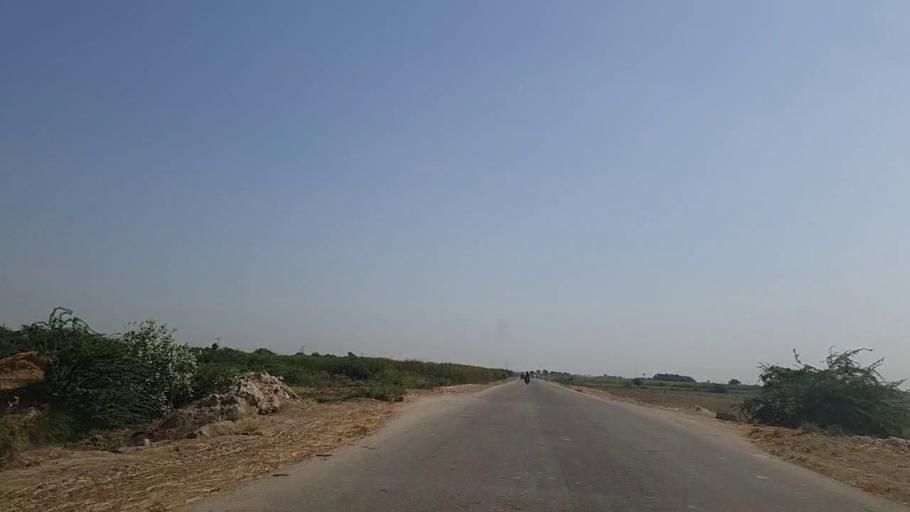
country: PK
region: Sindh
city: Mirpur Batoro
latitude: 24.7559
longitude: 68.2280
